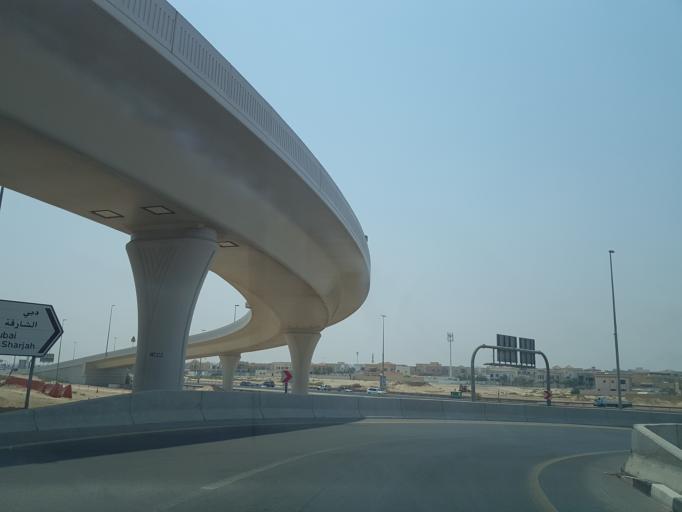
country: AE
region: Ash Shariqah
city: Sharjah
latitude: 25.2128
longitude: 55.4076
